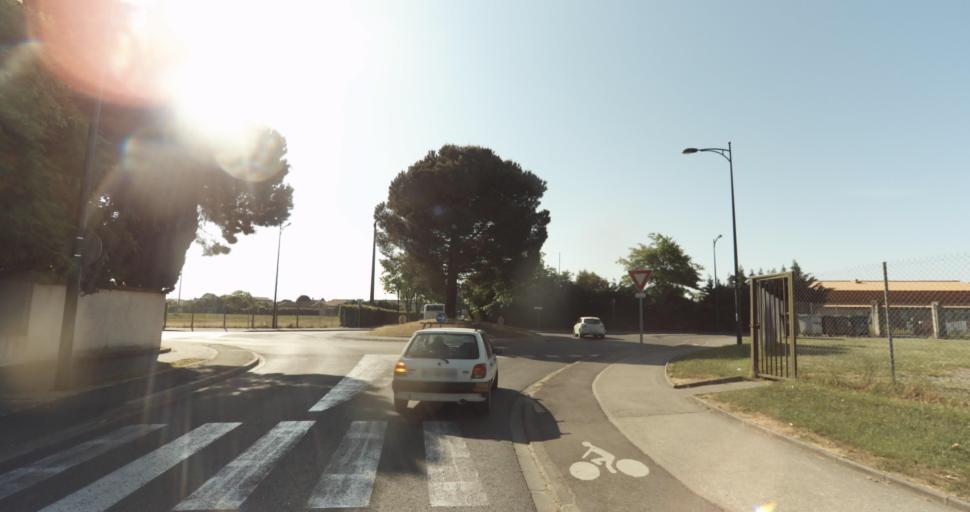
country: FR
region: Midi-Pyrenees
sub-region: Departement de la Haute-Garonne
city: Plaisance-du-Touch
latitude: 43.5651
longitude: 1.2885
